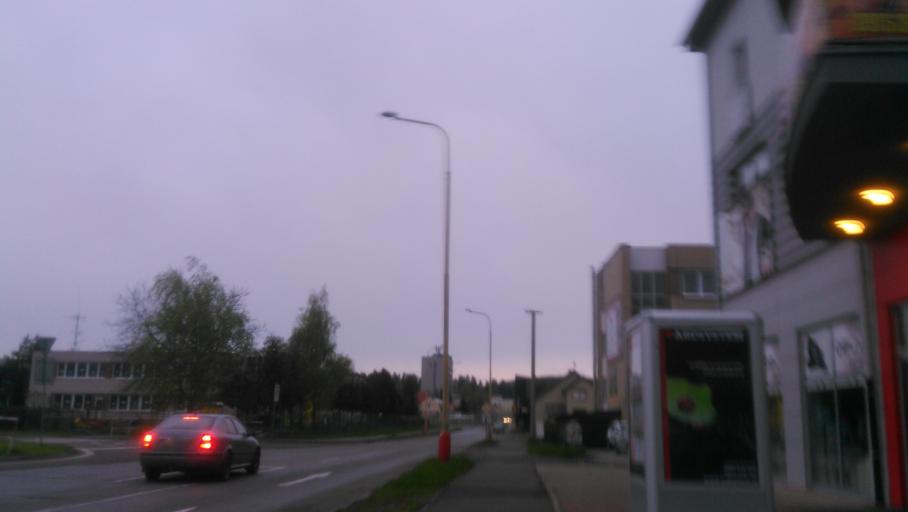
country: SK
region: Presovsky
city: Humenne
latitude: 48.9304
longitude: 21.9086
